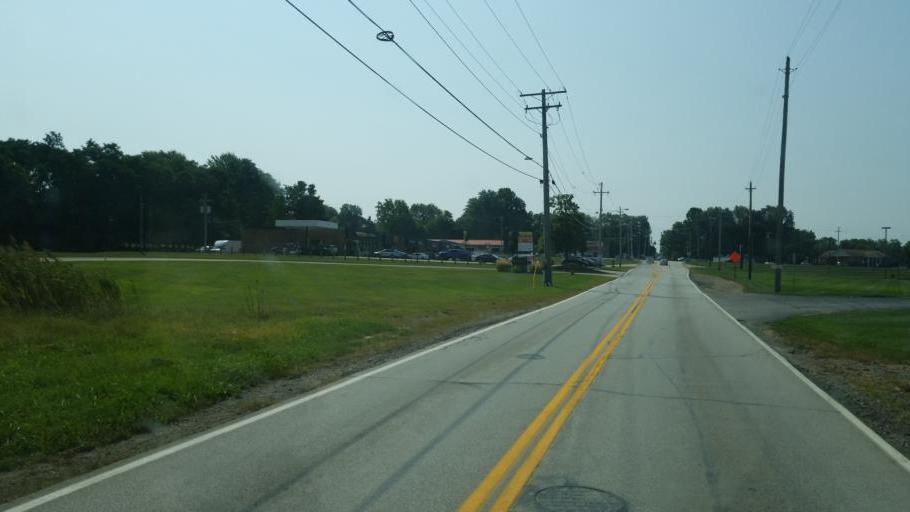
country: US
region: Ohio
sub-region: Lake County
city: Painesville
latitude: 41.7518
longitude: -81.2080
